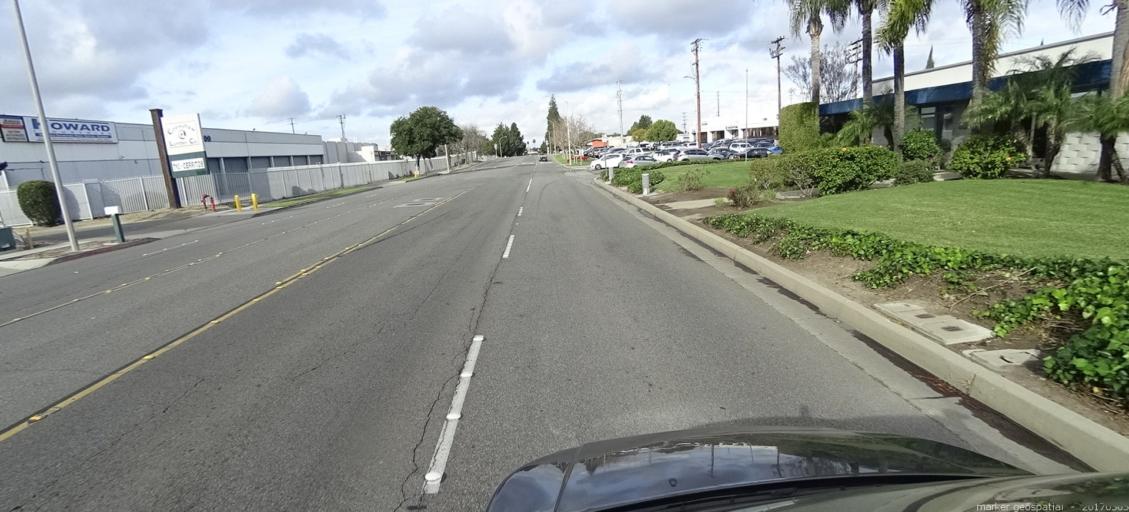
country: US
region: California
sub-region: Orange County
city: Anaheim
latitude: 33.8107
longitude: -117.8995
